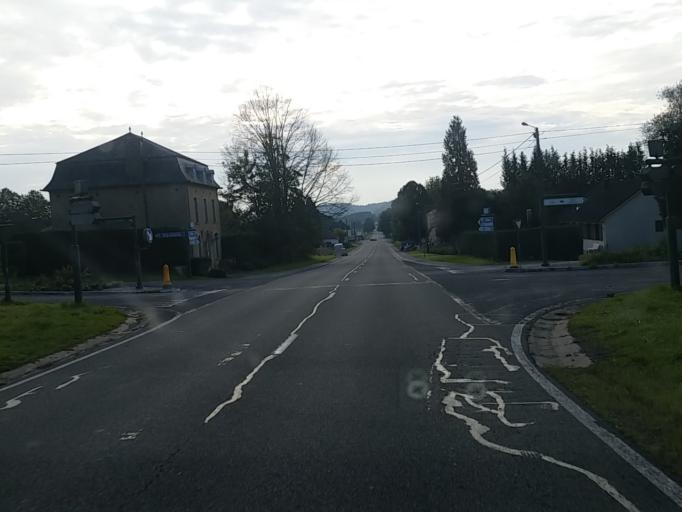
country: BE
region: Wallonia
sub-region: Province du Luxembourg
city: Herbeumont
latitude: 49.7284
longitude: 5.2362
